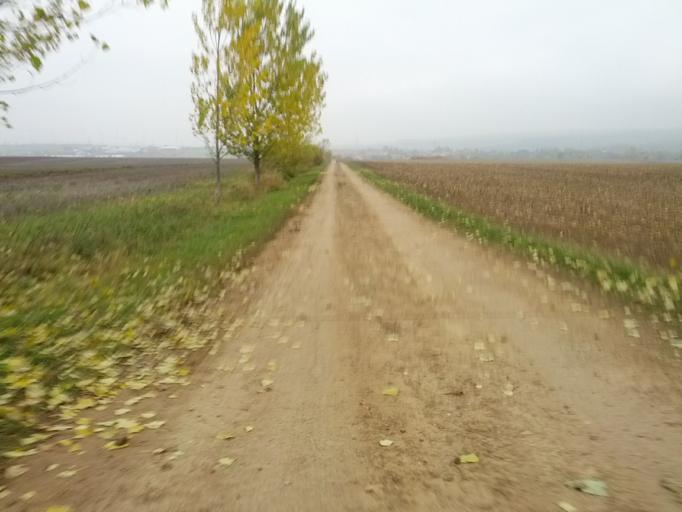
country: DE
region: Thuringia
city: Seebach
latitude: 50.9785
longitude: 10.4085
